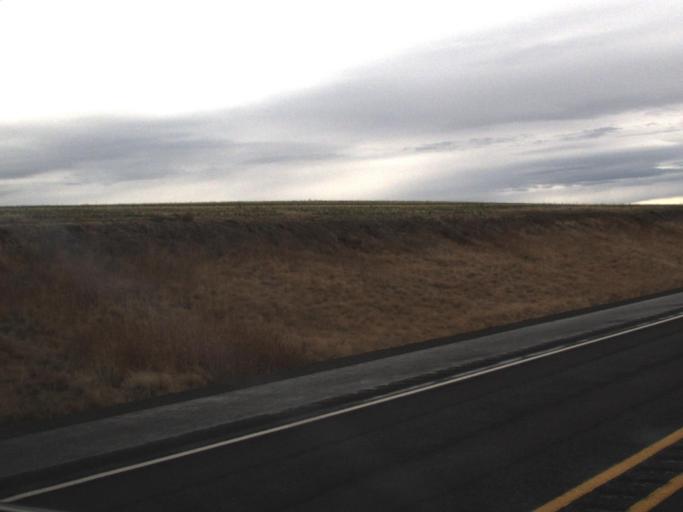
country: US
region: Washington
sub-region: Asotin County
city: Clarkston
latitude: 46.5227
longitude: -117.0830
